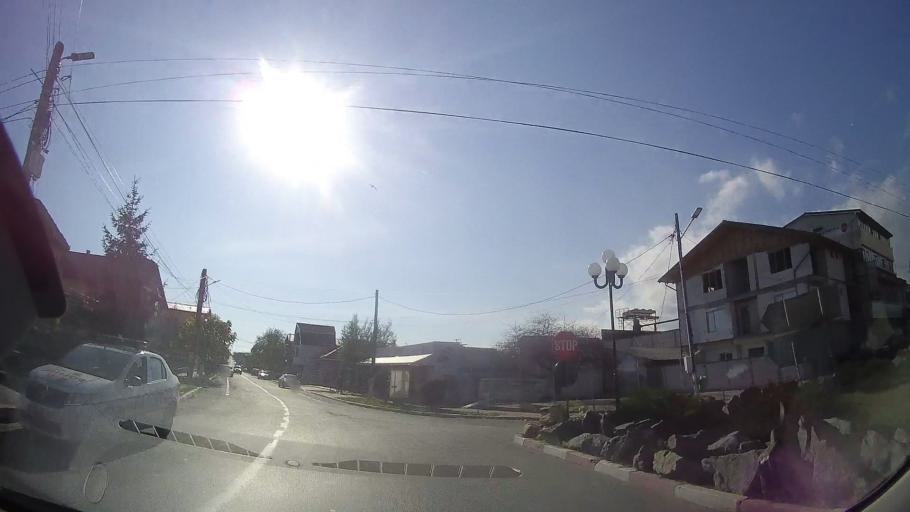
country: RO
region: Constanta
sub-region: Comuna Costinesti
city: Schitu
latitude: 43.9462
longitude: 28.6302
